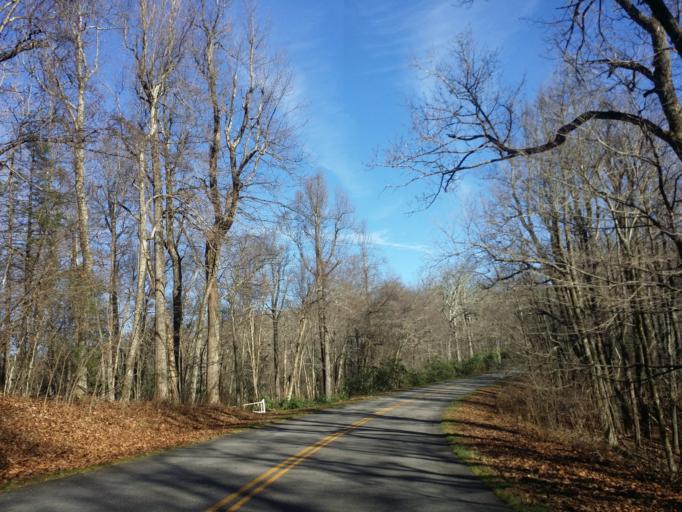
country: US
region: North Carolina
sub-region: Mitchell County
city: Spruce Pine
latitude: 35.8099
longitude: -82.1480
